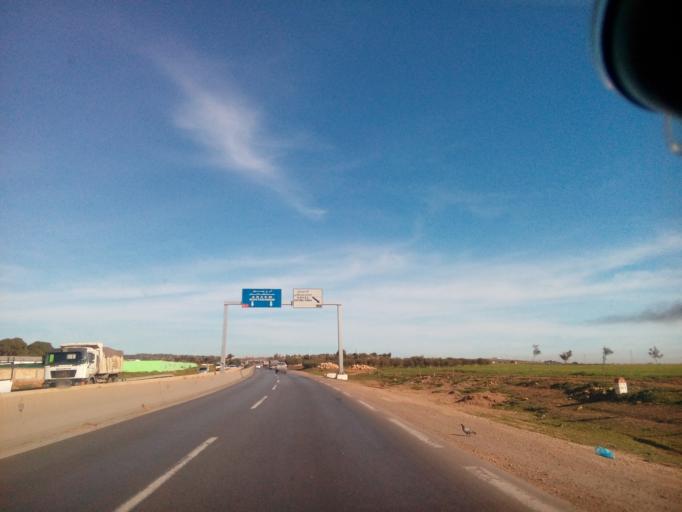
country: DZ
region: Oran
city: Ain el Bya
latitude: 35.7802
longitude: -0.4136
